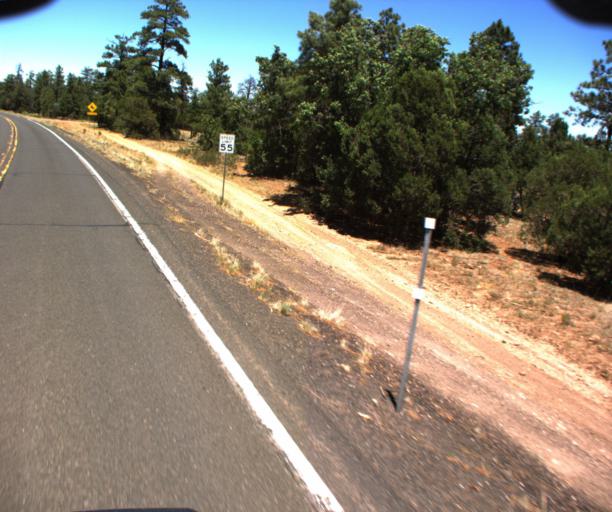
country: US
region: Arizona
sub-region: Gila County
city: Star Valley
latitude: 34.6513
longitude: -111.1084
